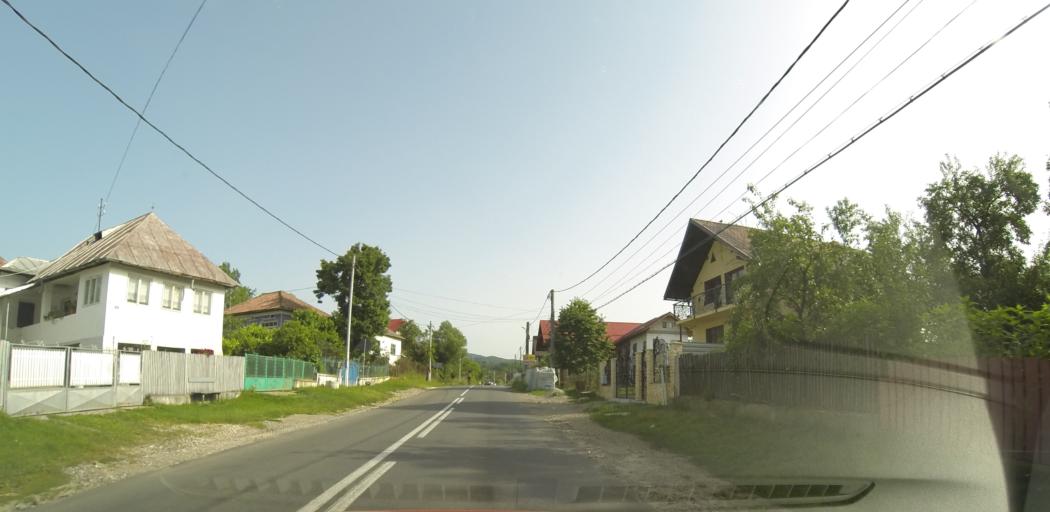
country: RO
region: Valcea
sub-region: Comuna Pausesti-Maglasi
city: Pausesti-Maglasi
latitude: 45.1471
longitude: 24.2458
